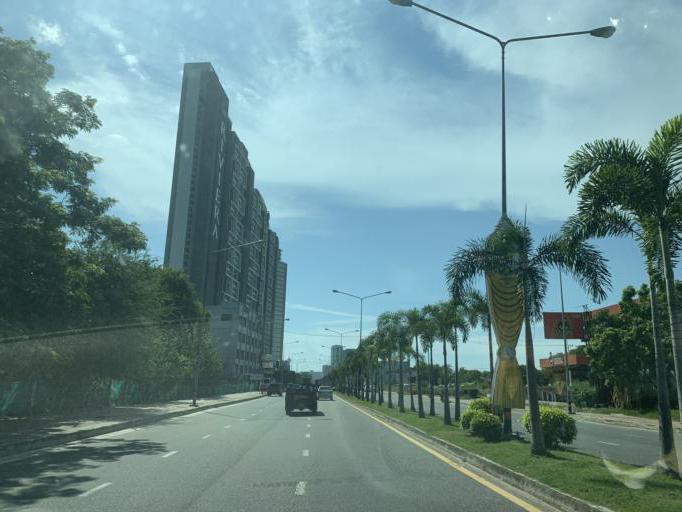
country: TH
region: Chon Buri
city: Phatthaya
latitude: 12.8812
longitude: 100.8877
